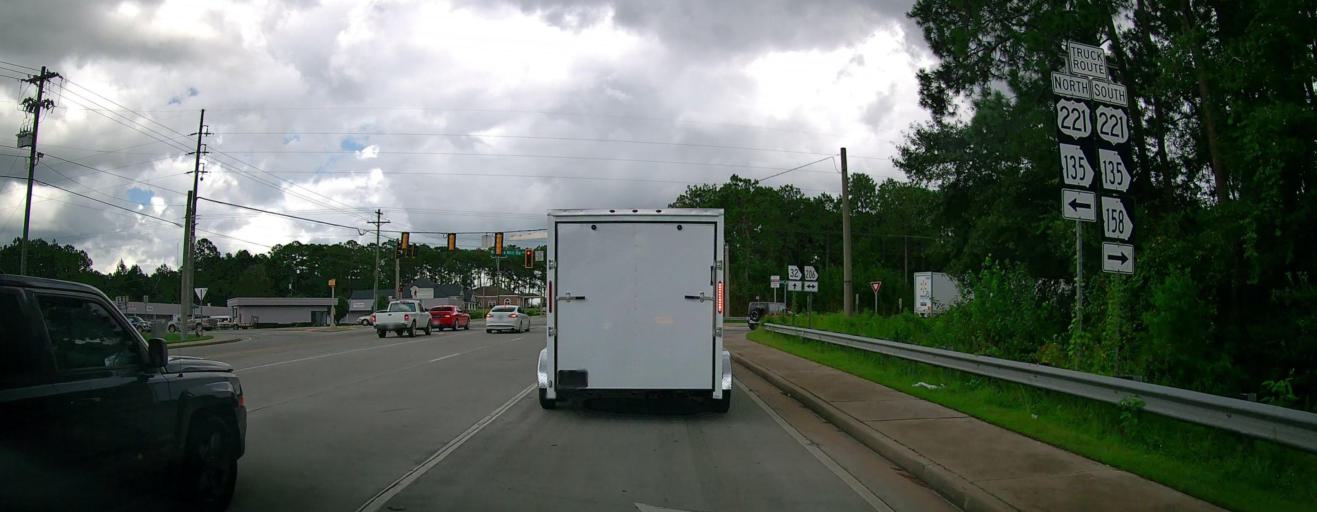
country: US
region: Georgia
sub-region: Coffee County
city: Douglas
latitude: 31.5127
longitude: -82.8718
